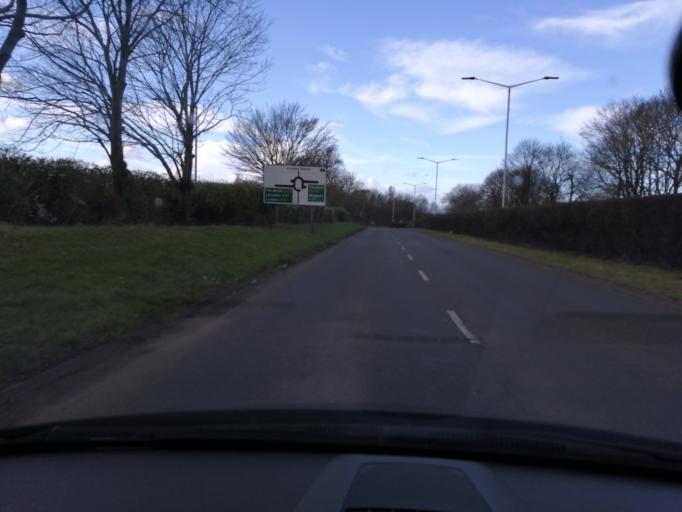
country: GB
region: England
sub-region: Peterborough
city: Peterborough
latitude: 52.5941
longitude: -0.2686
